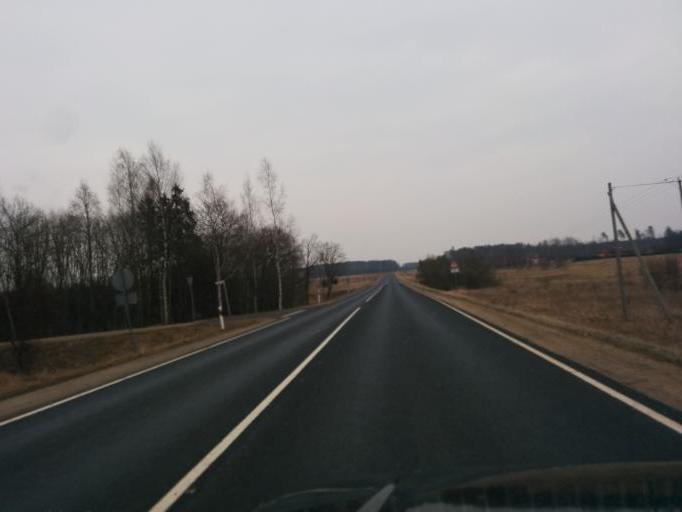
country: LV
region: Salaspils
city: Salaspils
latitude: 56.8261
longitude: 24.3566
